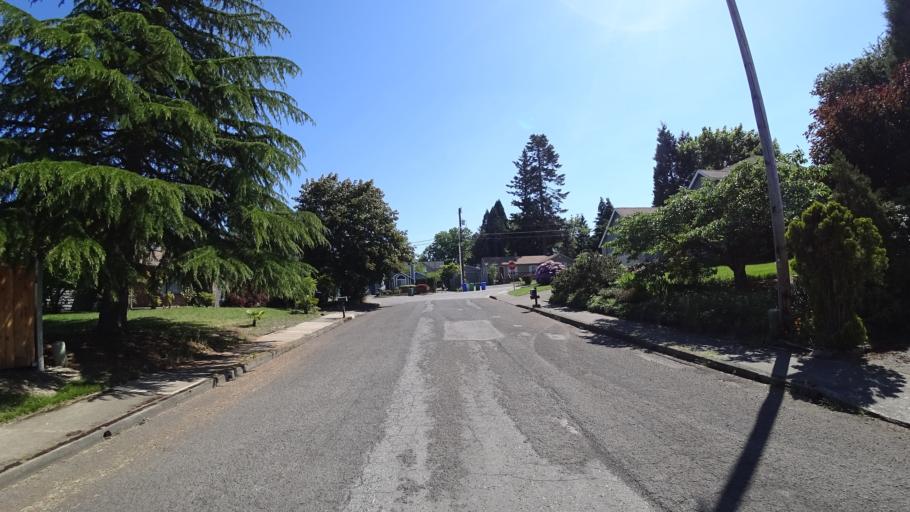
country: US
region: Oregon
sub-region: Washington County
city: Metzger
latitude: 45.4497
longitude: -122.7221
